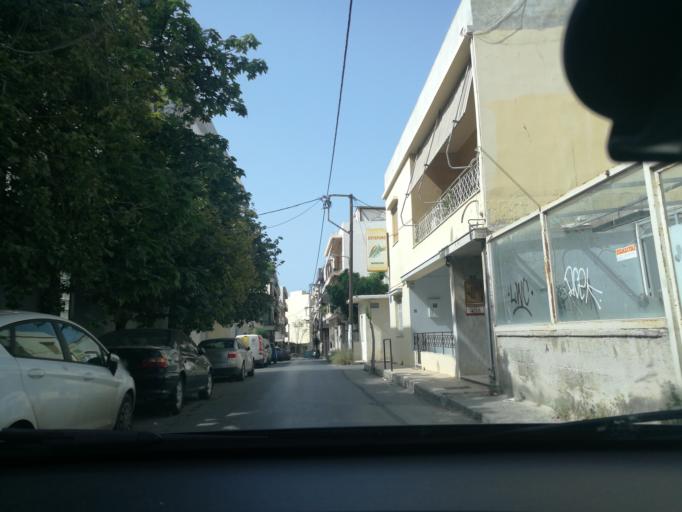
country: GR
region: Crete
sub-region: Nomos Irakleiou
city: Irakleion
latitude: 35.3278
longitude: 25.1307
